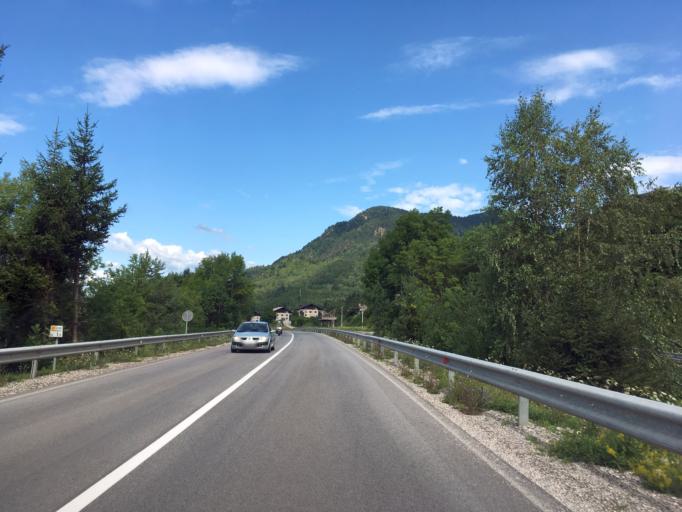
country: SI
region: Jesenice
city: Slovenski Javornik
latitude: 46.4239
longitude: 14.1008
